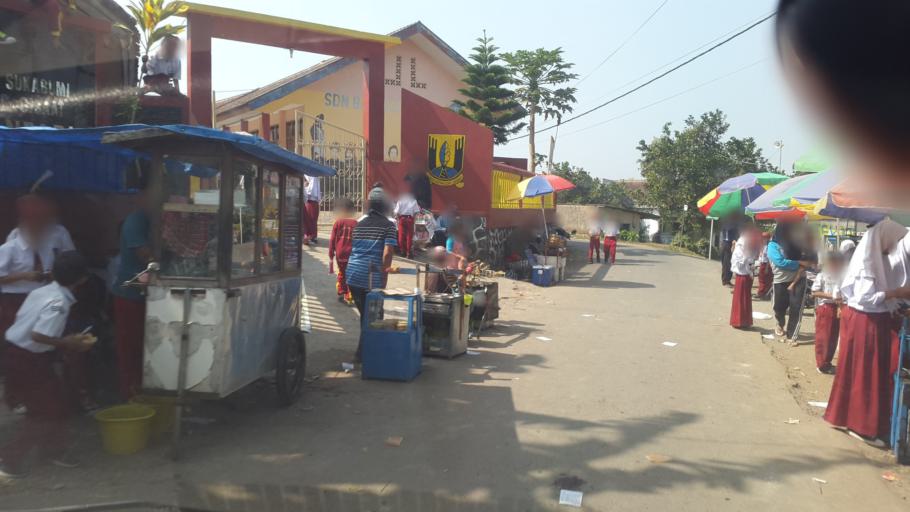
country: ID
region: West Java
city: Sukabumi
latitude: -6.8856
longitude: 106.9125
